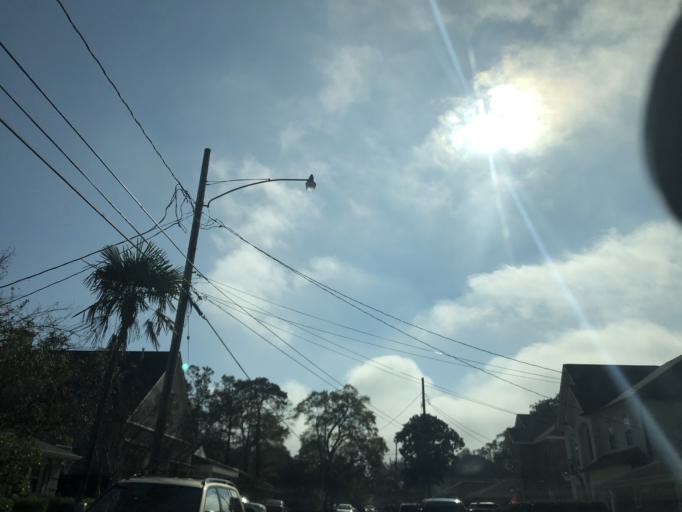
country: US
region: Louisiana
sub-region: Jefferson Parish
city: Metairie
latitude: 29.9849
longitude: -90.1520
